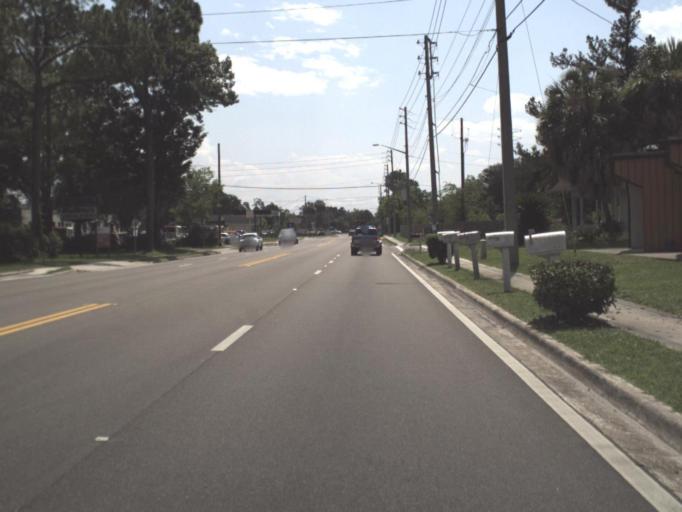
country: US
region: Florida
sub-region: Alachua County
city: Gainesville
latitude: 29.6738
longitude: -82.3014
